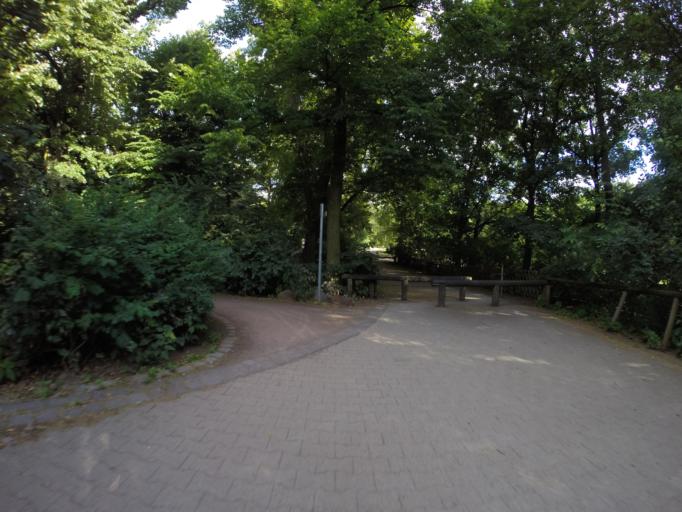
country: DE
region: Berlin
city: Friedenau
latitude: 52.4828
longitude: 13.3312
